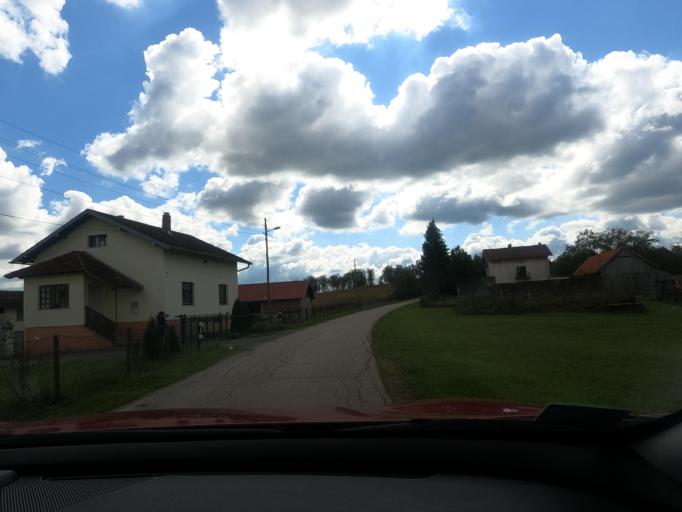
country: HR
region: Karlovacka
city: Vojnic
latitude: 45.2441
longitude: 15.7118
